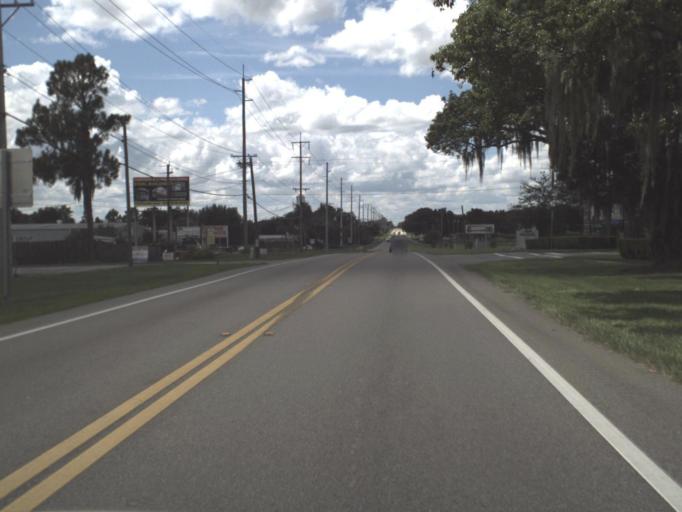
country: US
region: Florida
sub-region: Polk County
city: Cypress Gardens
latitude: 28.0225
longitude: -81.6805
